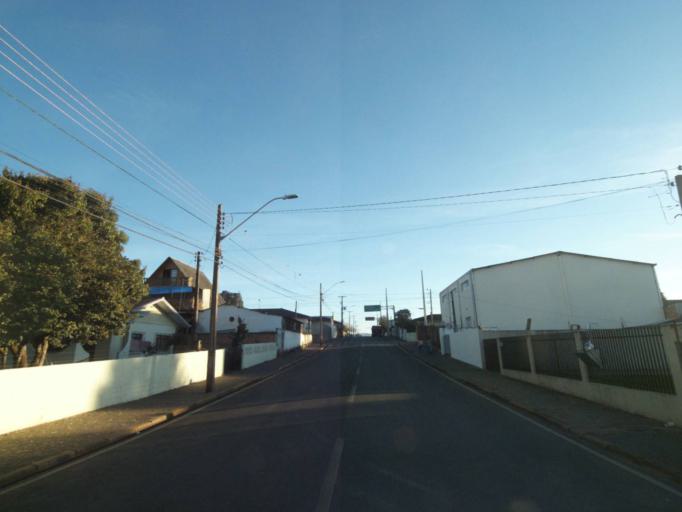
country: BR
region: Parana
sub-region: Tibagi
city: Tibagi
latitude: -24.5183
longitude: -50.4108
